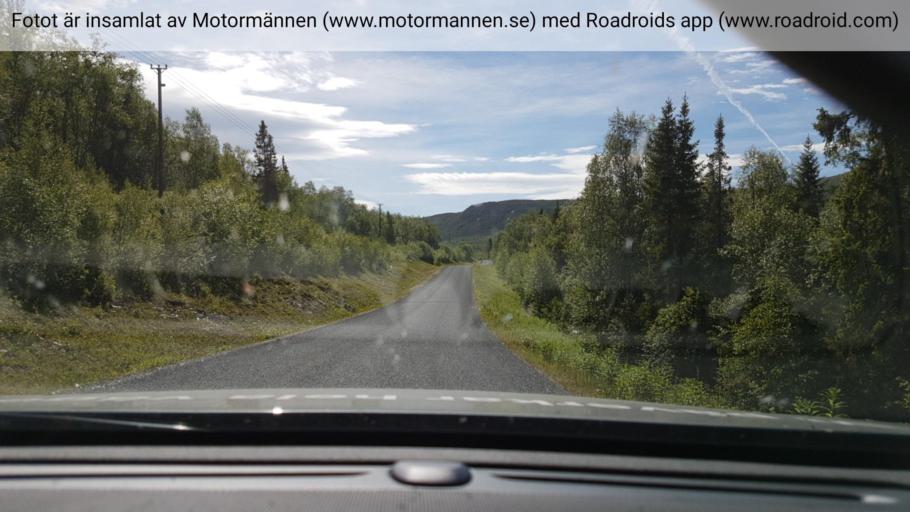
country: SE
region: Vaesterbotten
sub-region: Vilhelmina Kommun
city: Sjoberg
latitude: 65.2937
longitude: 15.2928
